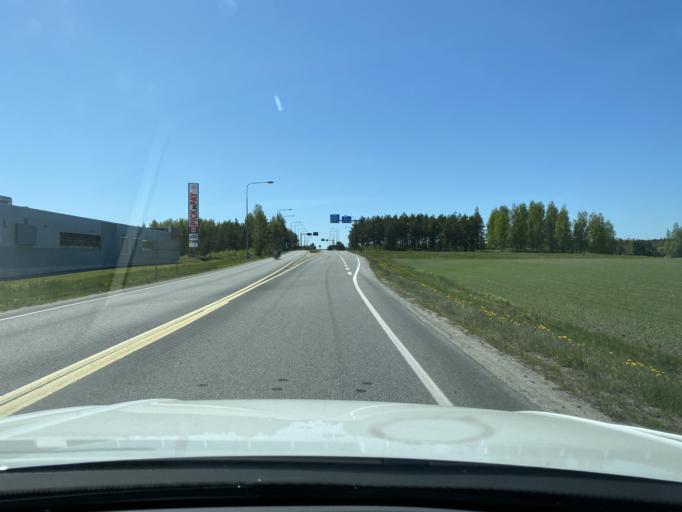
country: FI
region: Satakunta
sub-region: Pori
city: Huittinen
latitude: 61.1721
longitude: 22.6776
